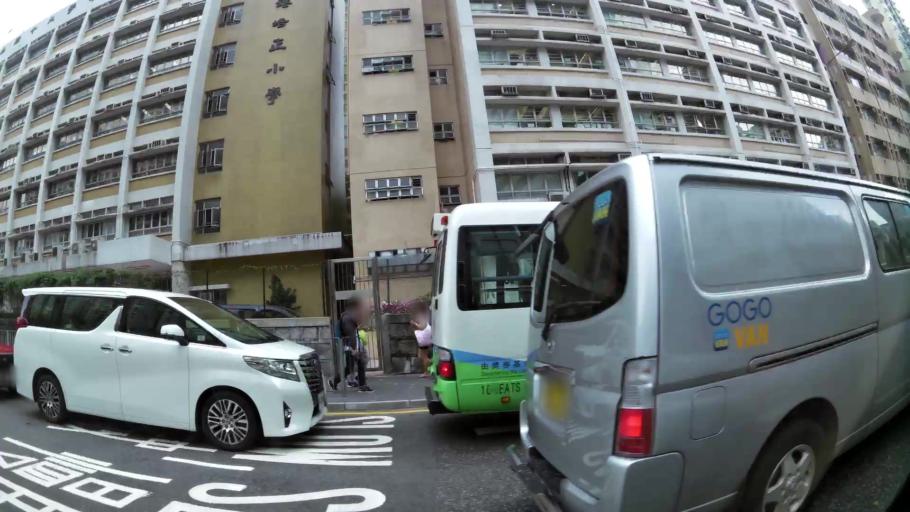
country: HK
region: Kowloon City
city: Kowloon
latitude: 22.3182
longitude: 114.1761
